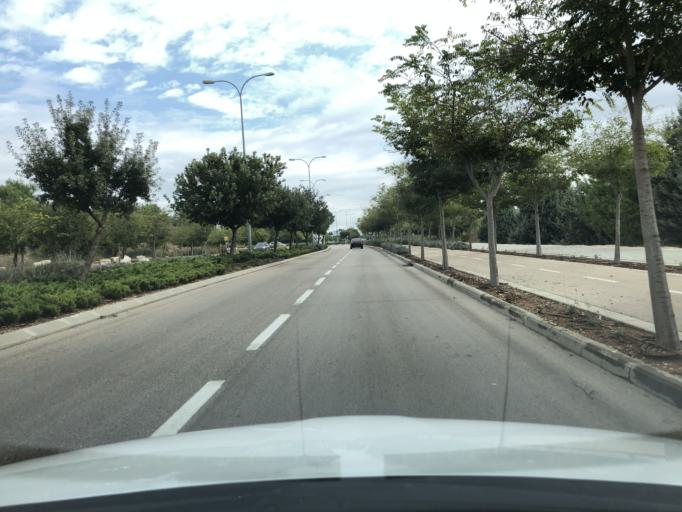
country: PS
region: West Bank
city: Al Midyah
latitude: 31.9230
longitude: 34.9979
